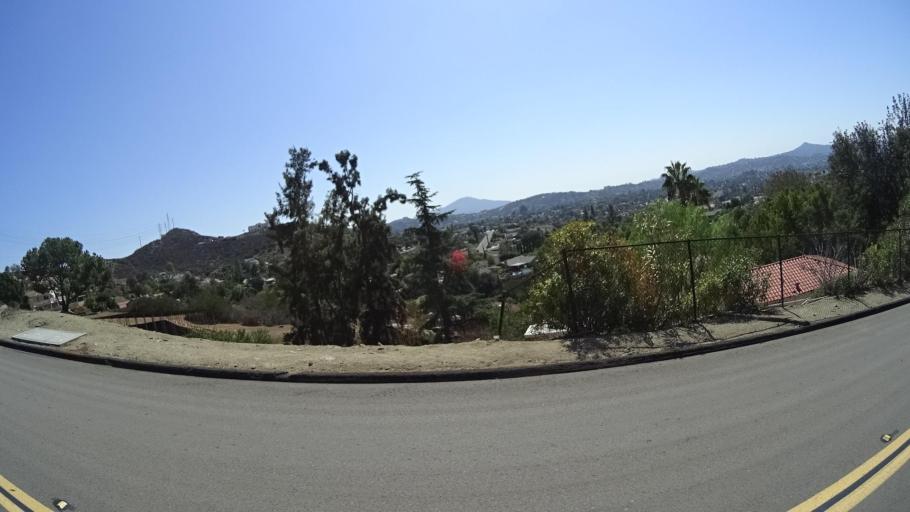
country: US
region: California
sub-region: San Diego County
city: Granite Hills
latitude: 32.8034
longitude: -116.8958
